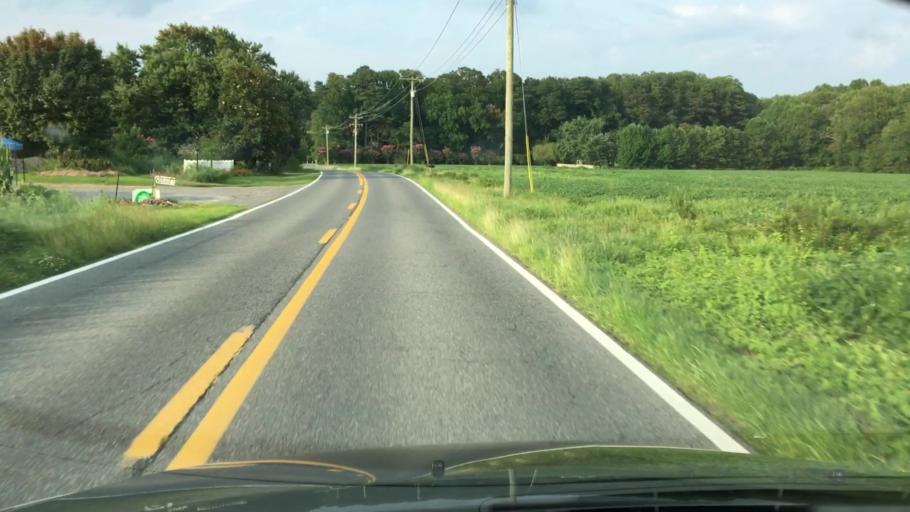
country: US
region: Delaware
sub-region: Sussex County
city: Ocean View
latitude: 38.4901
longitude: -75.1329
